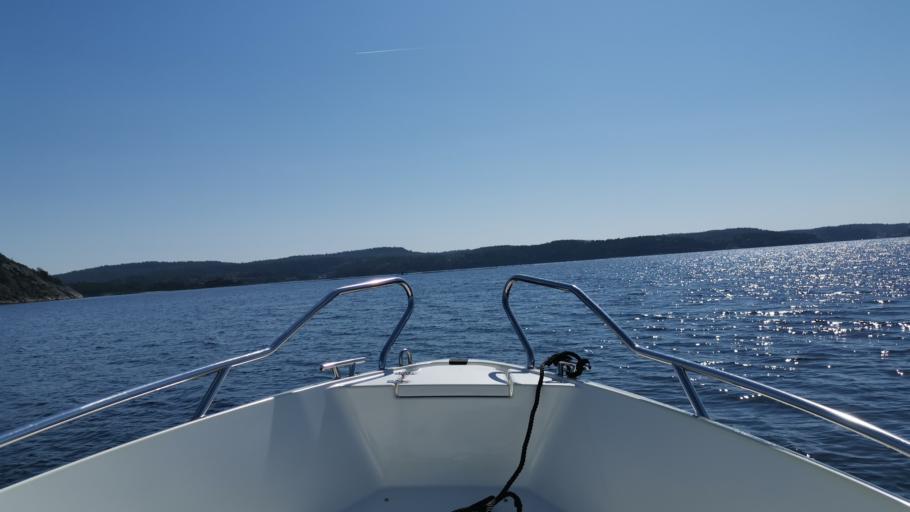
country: SE
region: Vaestra Goetaland
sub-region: Orust
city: Henan
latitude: 58.2496
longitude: 11.5765
